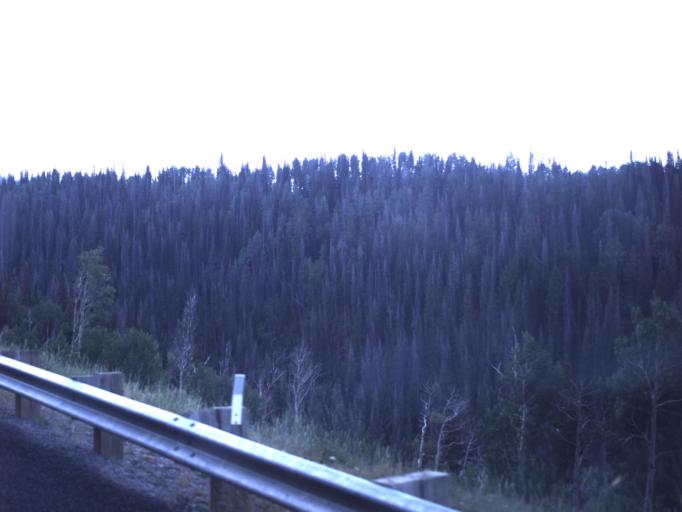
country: US
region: Utah
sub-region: Summit County
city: Francis
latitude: 40.5056
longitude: -111.0451
